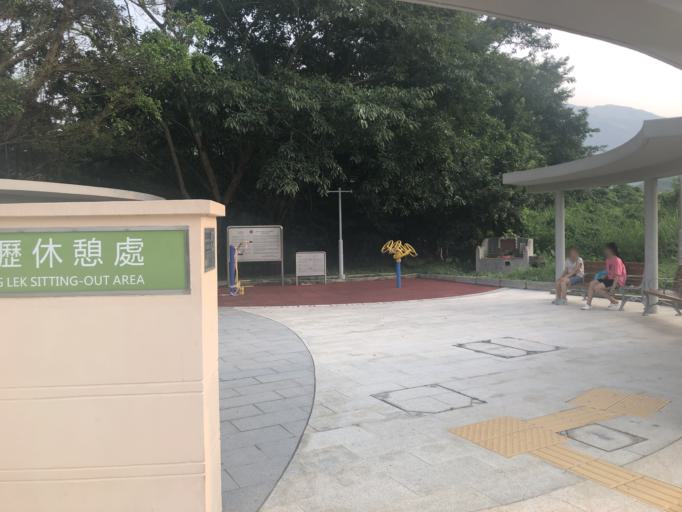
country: CN
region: Guangdong
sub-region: Shenzhen
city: Shenzhen
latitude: 22.4854
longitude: 114.1027
